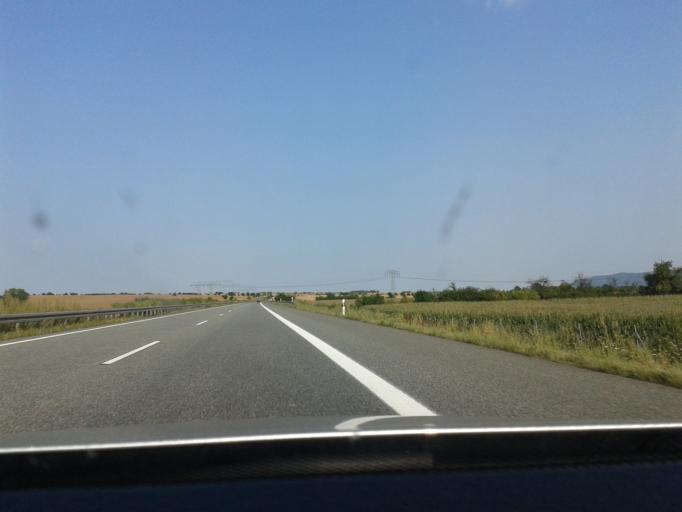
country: DE
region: Thuringia
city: Gorsbach
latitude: 51.4698
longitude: 10.9215
